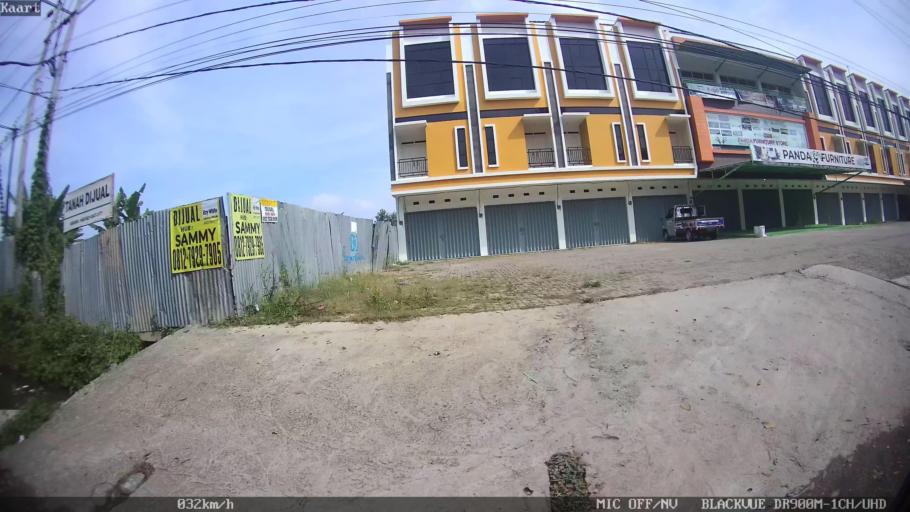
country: ID
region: Lampung
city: Kedaton
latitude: -5.3762
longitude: 105.3064
